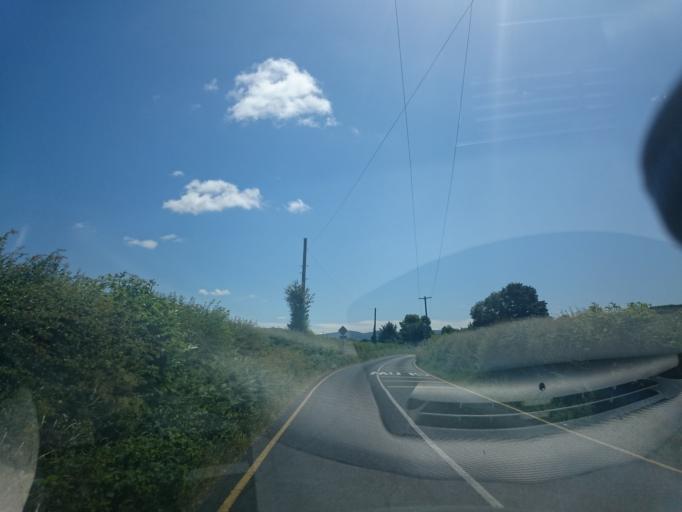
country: IE
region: Leinster
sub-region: Kilkenny
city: Graiguenamanagh
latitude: 52.5888
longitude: -6.9617
